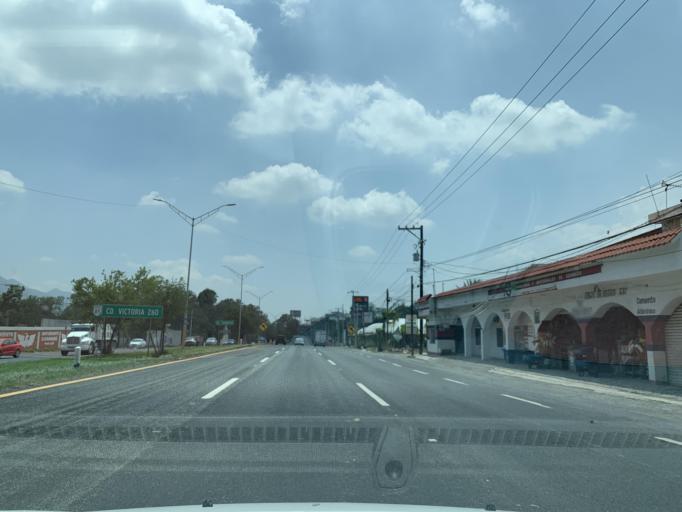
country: MX
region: Nuevo Leon
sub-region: Juarez
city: Bosques de San Pedro
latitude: 25.5181
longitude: -100.2009
